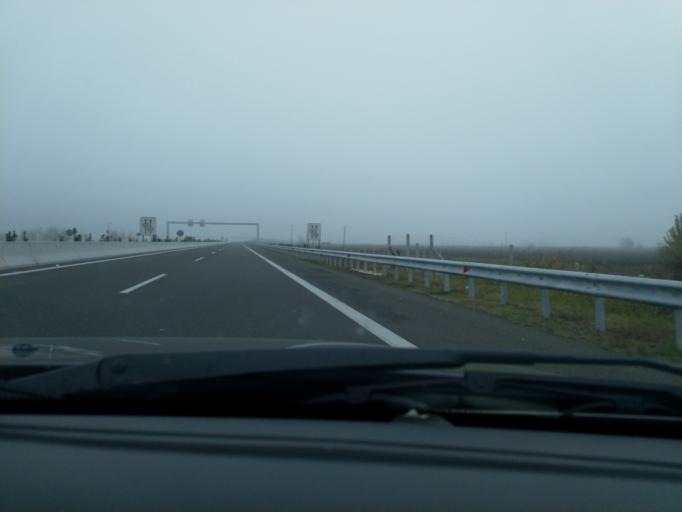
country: GR
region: Thessaly
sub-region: Nomos Kardhitsas
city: Anavra
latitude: 39.2590
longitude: 22.0837
